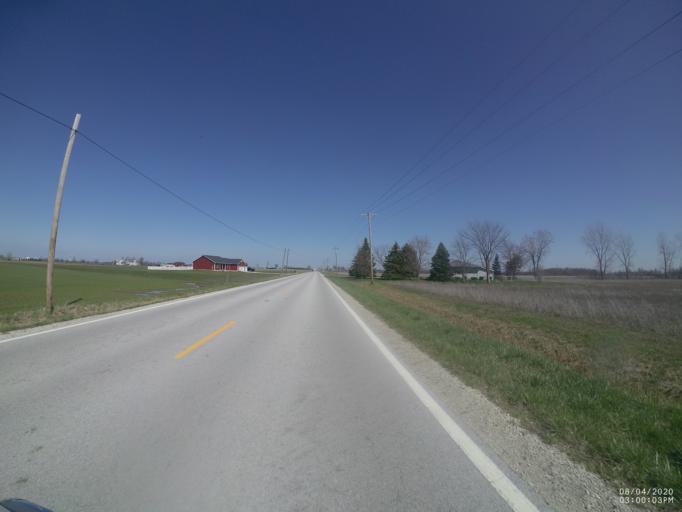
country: US
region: Ohio
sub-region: Sandusky County
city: Stony Prairie
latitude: 41.3226
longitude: -83.2433
